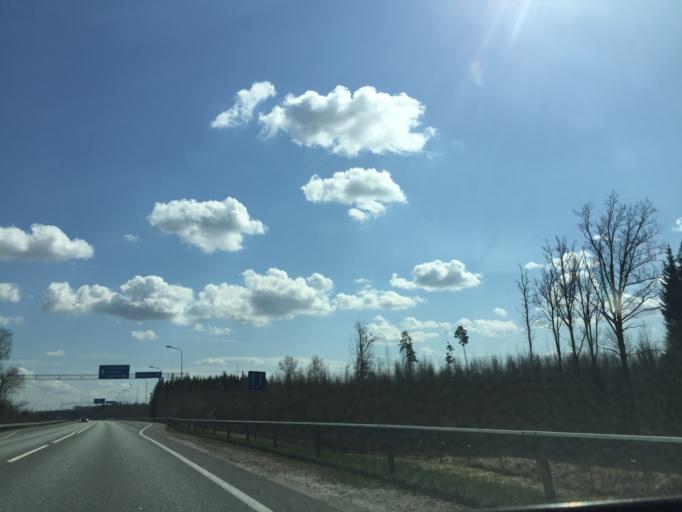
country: LV
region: Kegums
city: Kegums
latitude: 56.8260
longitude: 24.7528
